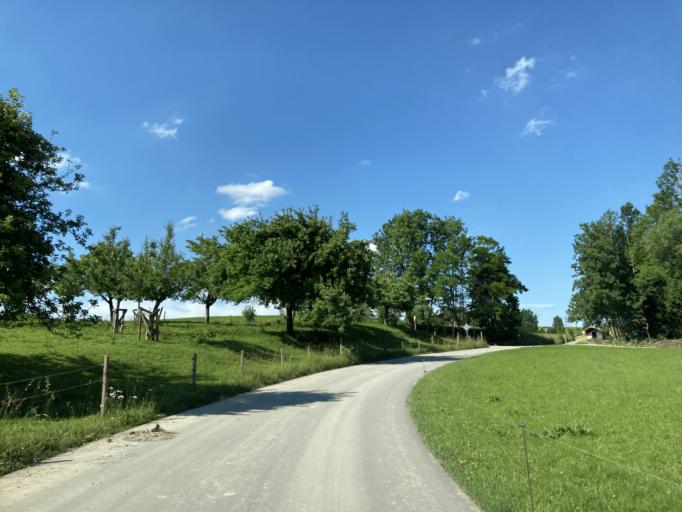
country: DE
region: Bavaria
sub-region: Upper Bavaria
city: Samerberg
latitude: 47.7603
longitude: 12.2171
